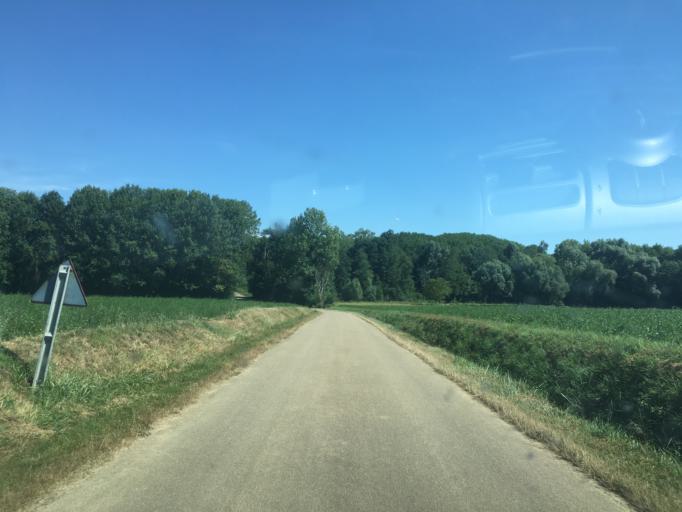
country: FR
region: Bourgogne
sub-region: Departement de l'Yonne
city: Fleury-la-Vallee
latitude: 47.8679
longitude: 3.4387
